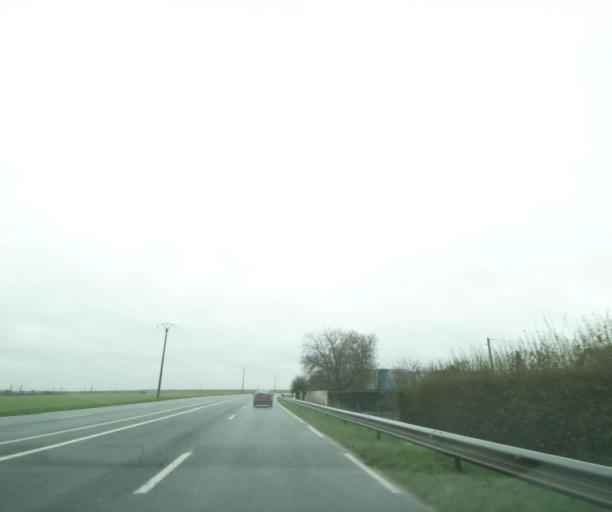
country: FR
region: Centre
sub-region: Departement du Loiret
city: Chevilly
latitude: 48.0515
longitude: 1.8755
